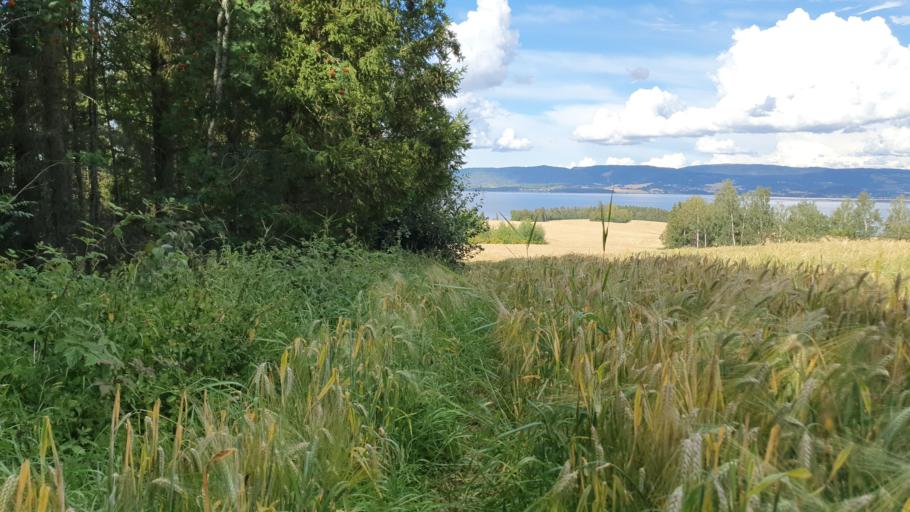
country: NO
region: Nord-Trondelag
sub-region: Levanger
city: Levanger
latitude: 63.7728
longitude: 11.3782
